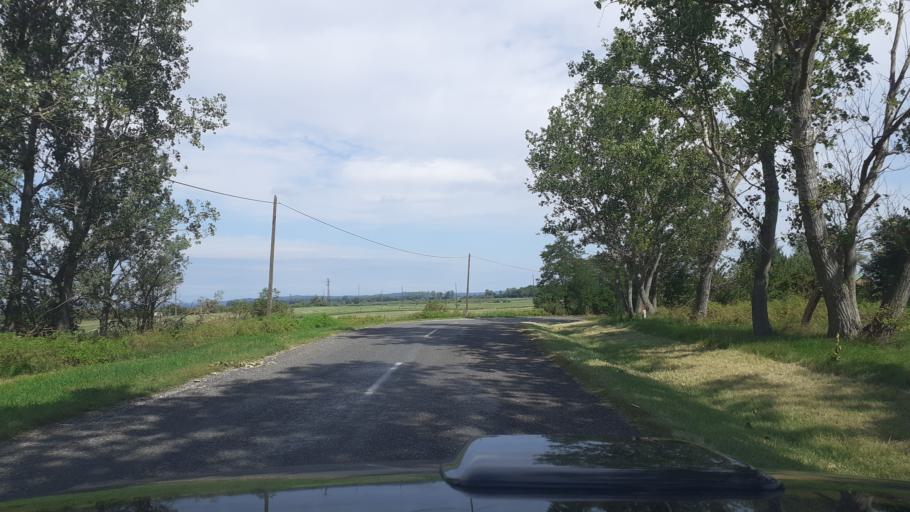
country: HU
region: Fejer
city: Seregelyes
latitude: 47.1326
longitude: 18.5753
